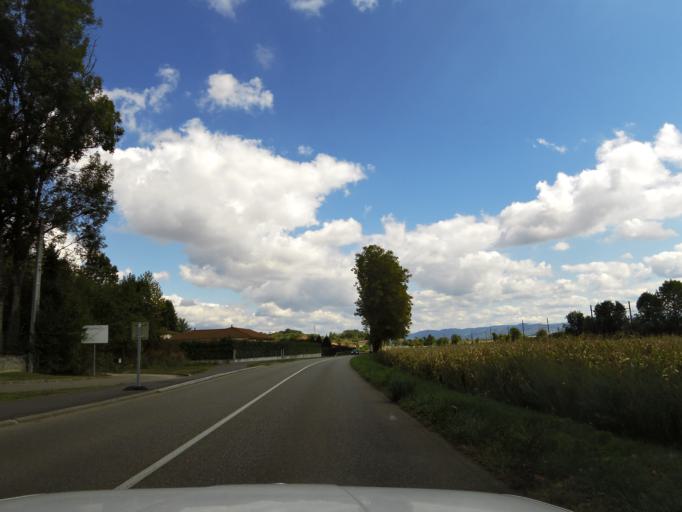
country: FR
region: Rhone-Alpes
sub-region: Departement de l'Ain
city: Meximieux
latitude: 45.9062
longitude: 5.2041
